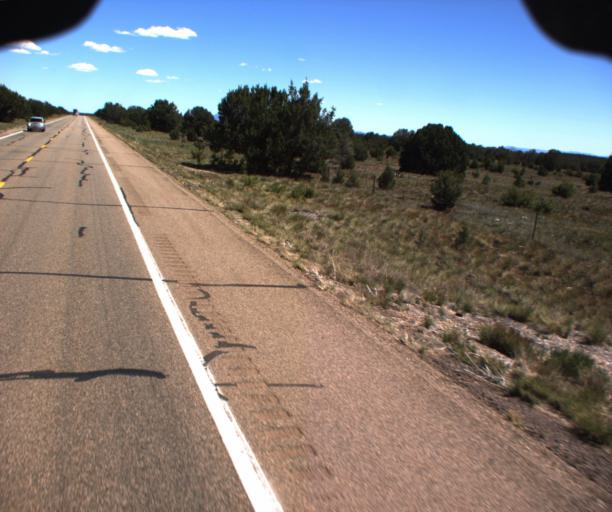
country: US
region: Arizona
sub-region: Yavapai County
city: Paulden
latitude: 35.0928
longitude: -112.4172
